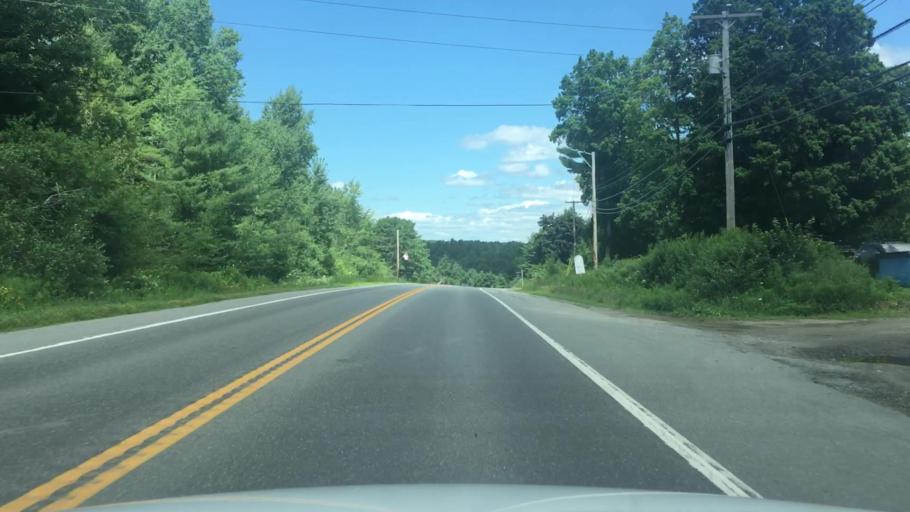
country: US
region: Maine
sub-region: Waldo County
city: Belfast
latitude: 44.3892
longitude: -68.9901
